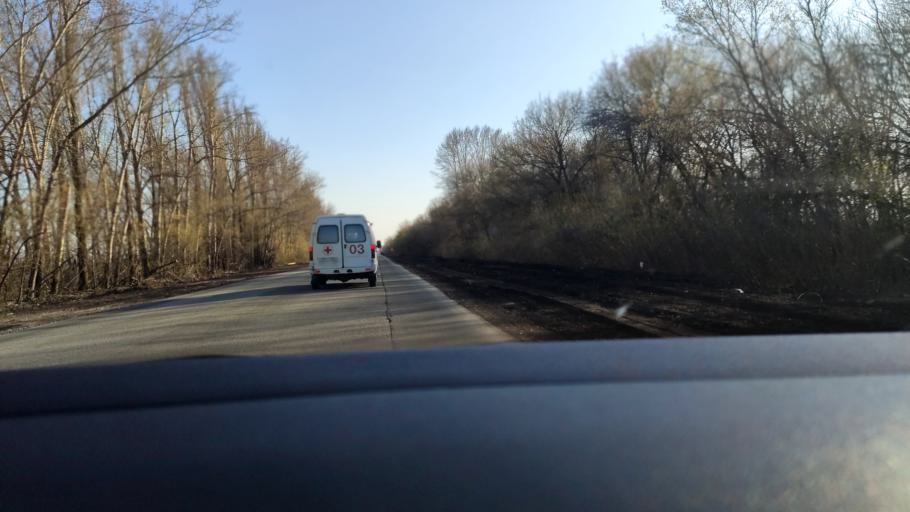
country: RU
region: Voronezj
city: Uryv-Pokrovka
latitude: 51.1675
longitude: 39.0728
